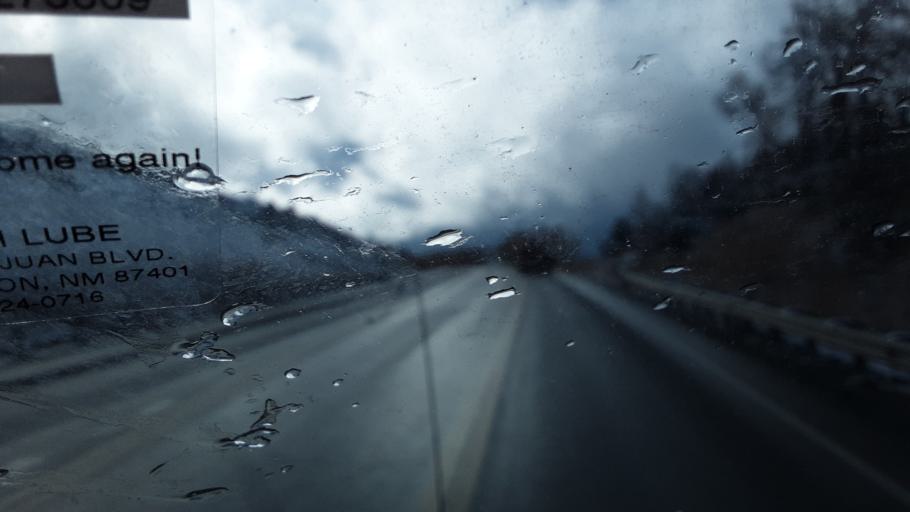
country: US
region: Colorado
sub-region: La Plata County
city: Bayfield
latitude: 37.2294
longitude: -107.6080
